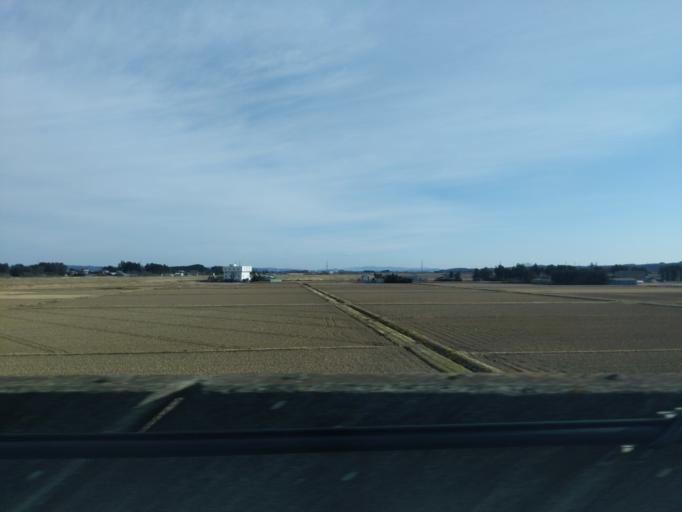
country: JP
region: Miyagi
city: Furukawa
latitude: 38.5383
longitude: 140.9611
